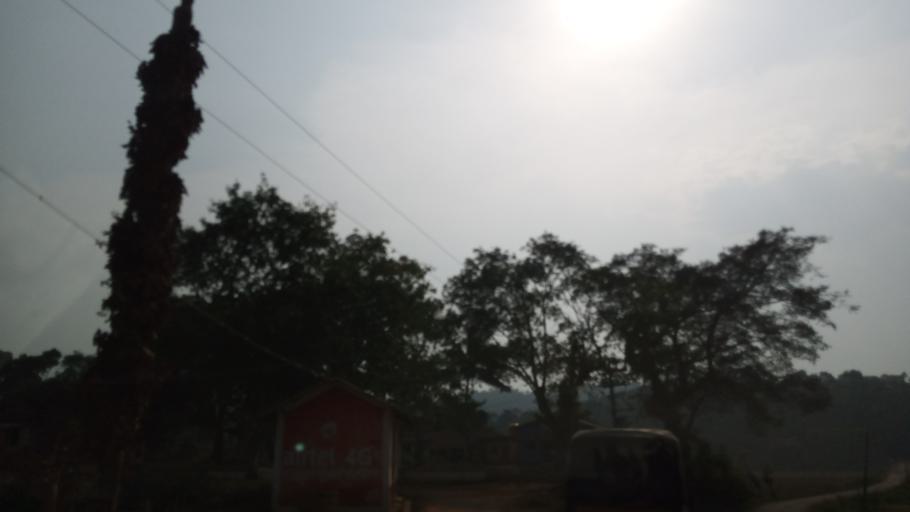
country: IN
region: Karnataka
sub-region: Chikmagalur
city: Mudigere
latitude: 13.0557
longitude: 75.6582
